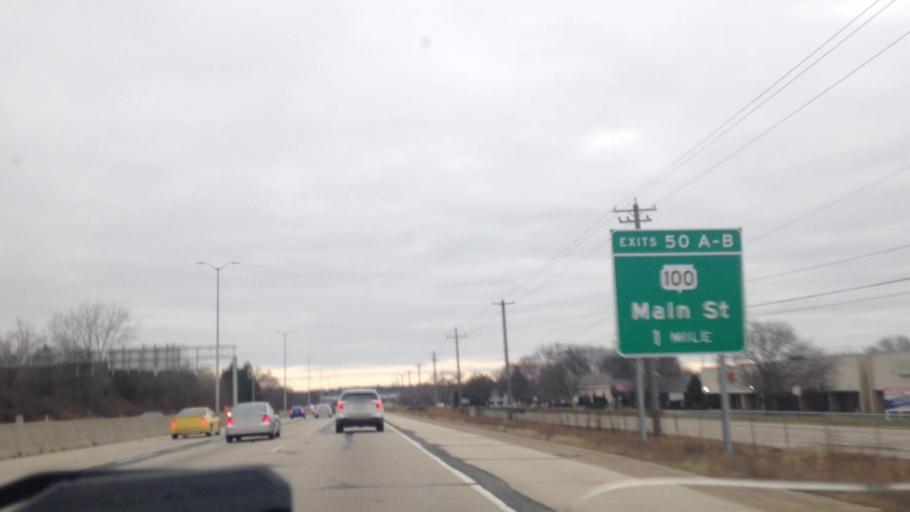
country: US
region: Wisconsin
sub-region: Waukesha County
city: Menomonee Falls
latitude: 43.1675
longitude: -88.0743
